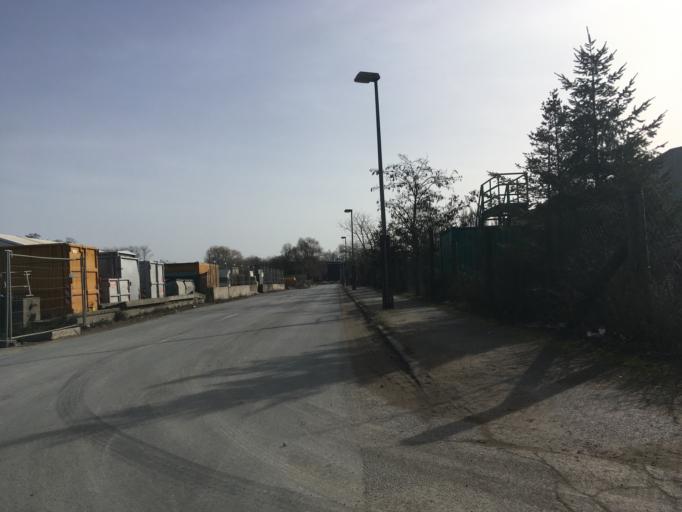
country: DE
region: Berlin
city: Kopenick Bezirk
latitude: 52.4333
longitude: 13.5670
